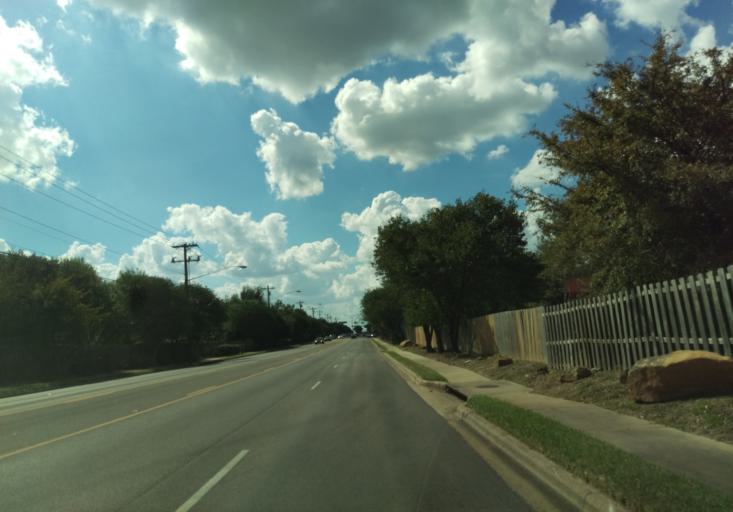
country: US
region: Texas
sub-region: Brazos County
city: College Station
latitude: 30.5770
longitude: -96.3020
